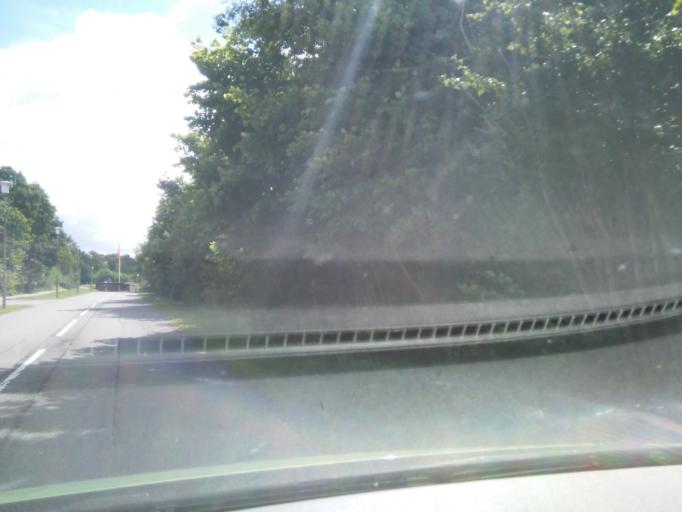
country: DK
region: Central Jutland
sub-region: Arhus Kommune
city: Logten
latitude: 56.2541
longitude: 10.3402
